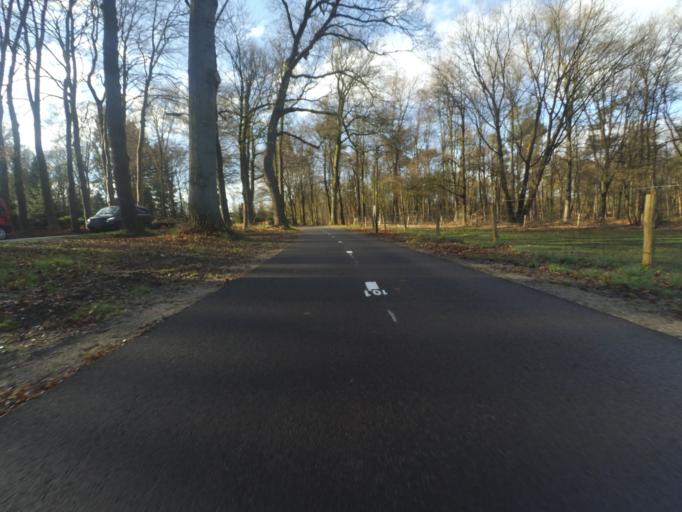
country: NL
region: Gelderland
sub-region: Gemeente Apeldoorn
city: Beekbergen
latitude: 52.1211
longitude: 5.8726
